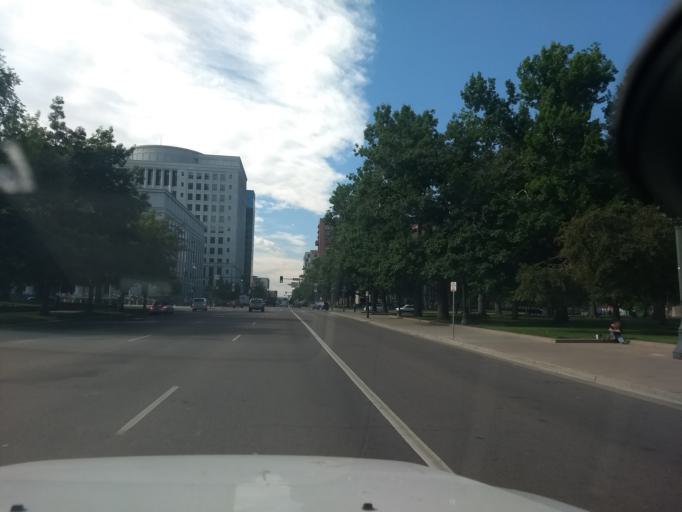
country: US
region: Colorado
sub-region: Denver County
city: Denver
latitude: 39.7393
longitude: -104.9874
